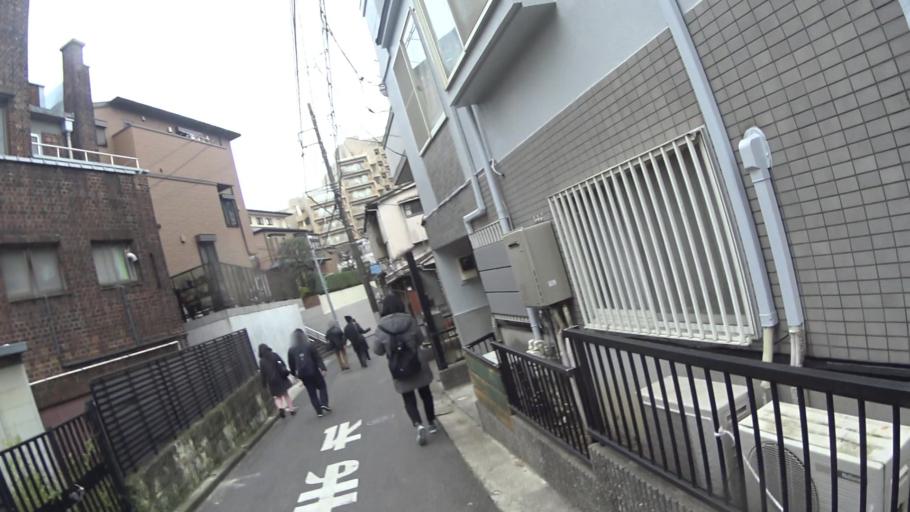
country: JP
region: Kanagawa
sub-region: Kawasaki-shi
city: Kawasaki
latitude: 35.5870
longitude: 139.7248
